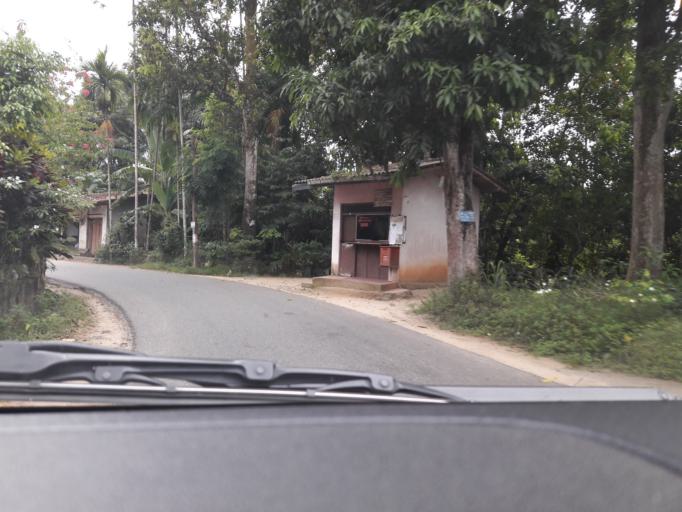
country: LK
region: Southern
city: Galle
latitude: 6.1819
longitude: 80.2997
